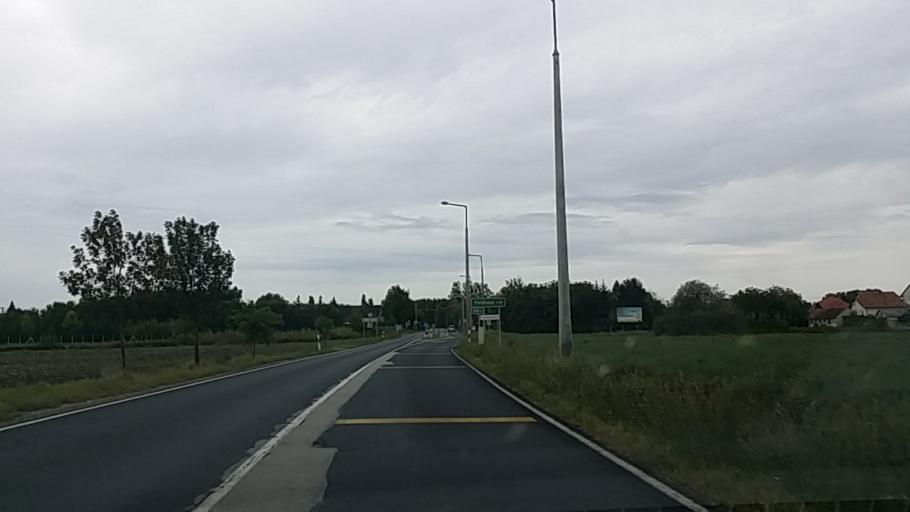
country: HU
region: Gyor-Moson-Sopron
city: Fertoszentmiklos
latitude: 47.5904
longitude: 16.8890
